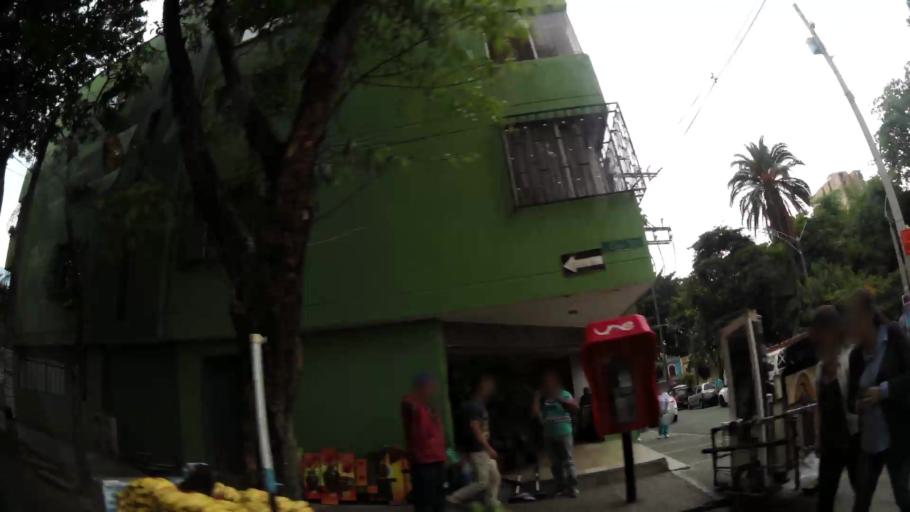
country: CO
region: Antioquia
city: Medellin
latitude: 6.2482
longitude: -75.5571
